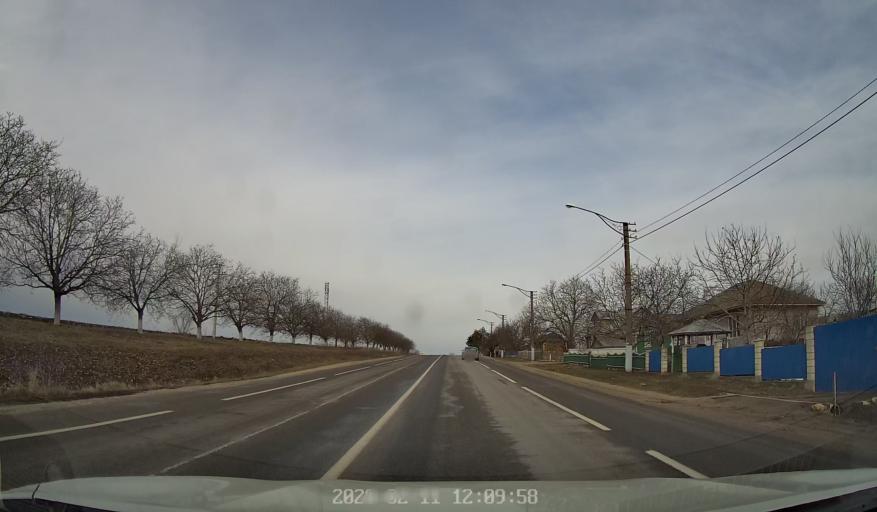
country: MD
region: Riscani
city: Riscani
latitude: 48.0357
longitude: 27.5311
